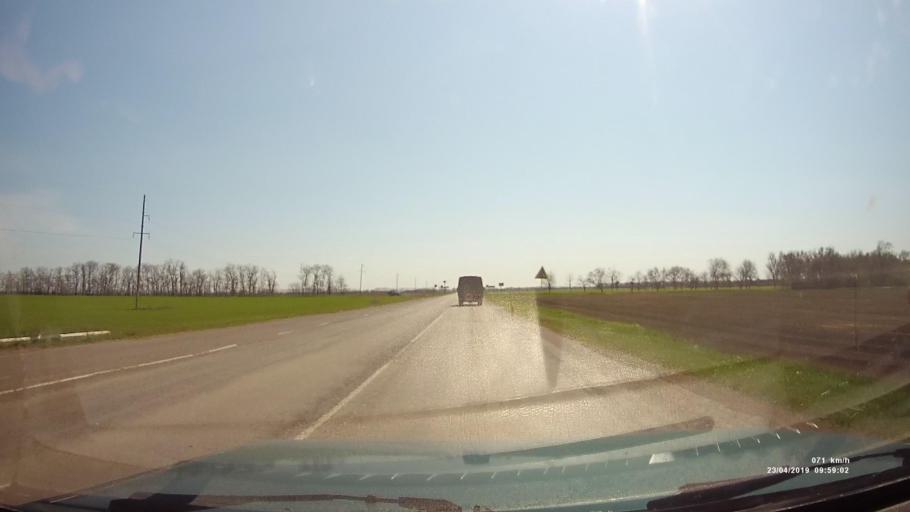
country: RU
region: Rostov
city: Sovetskoye
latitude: 46.7764
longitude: 42.1089
